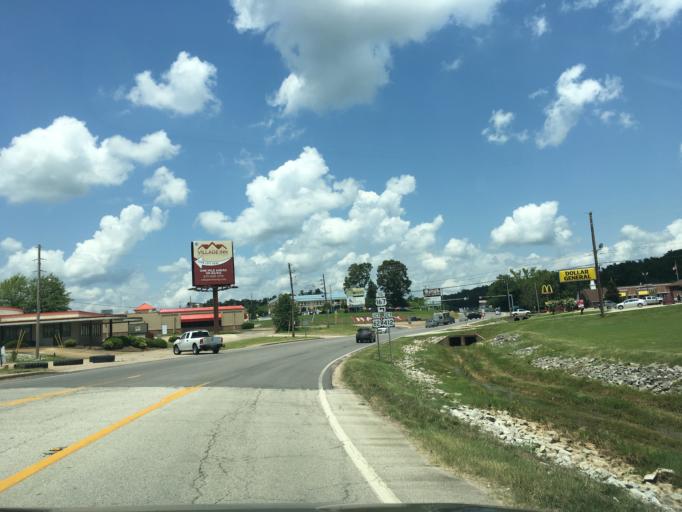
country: US
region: Arkansas
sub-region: Sharp County
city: Cherokee Village
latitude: 36.3160
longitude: -91.4866
